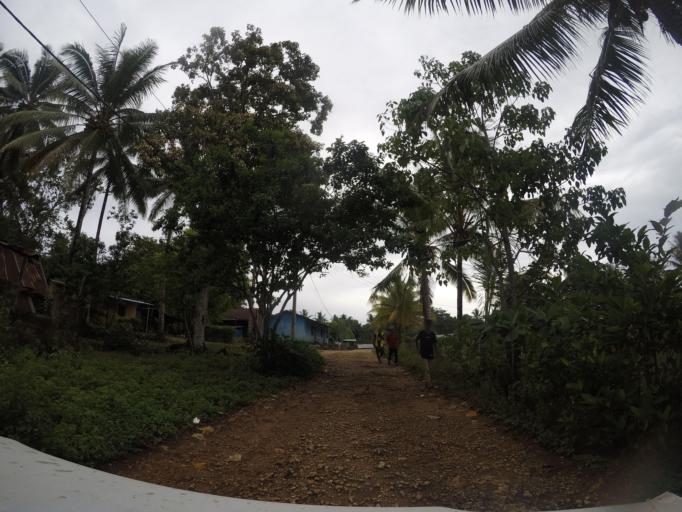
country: TL
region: Lautem
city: Lospalos
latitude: -8.5329
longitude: 126.9986
